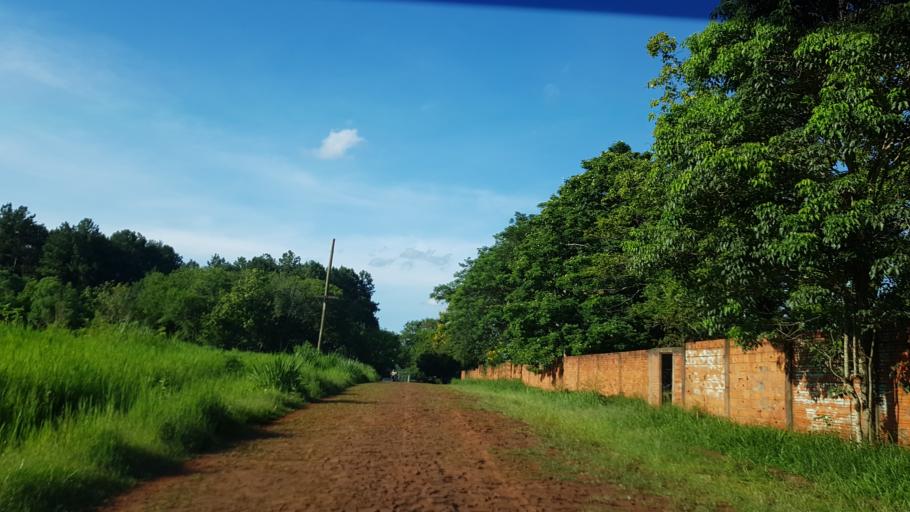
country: AR
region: Misiones
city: Puerto Libertad
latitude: -25.9231
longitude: -54.5898
